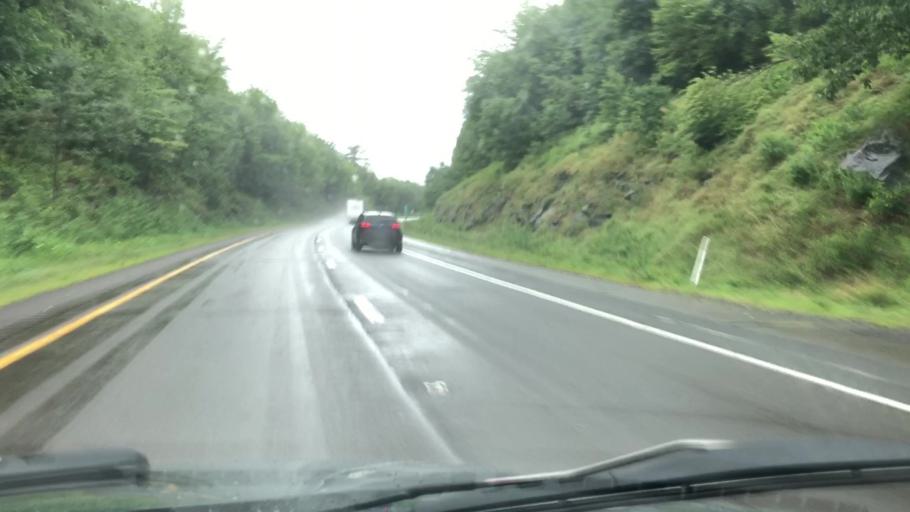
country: US
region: Pennsylvania
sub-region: Pike County
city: Conashaugh Lakes
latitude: 41.3471
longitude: -74.9902
